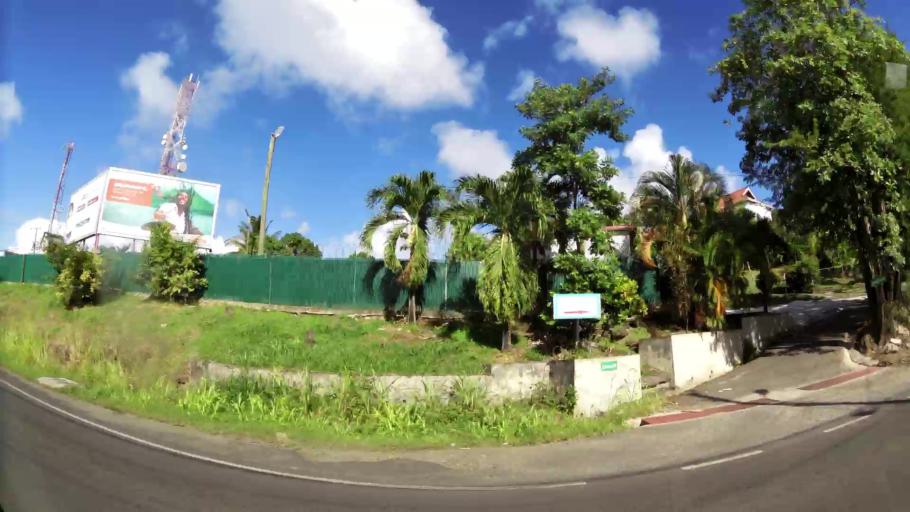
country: LC
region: Castries Quarter
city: Bisee
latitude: 14.0446
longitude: -60.9693
